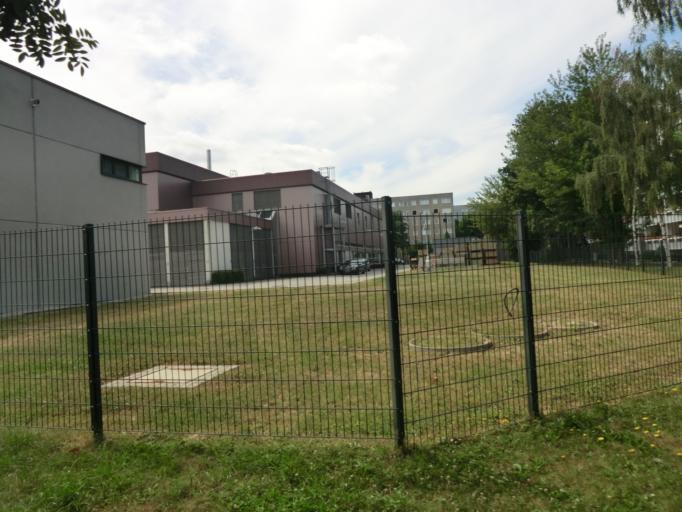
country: DE
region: Saxony
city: Dresden
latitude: 51.0353
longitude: 13.7384
